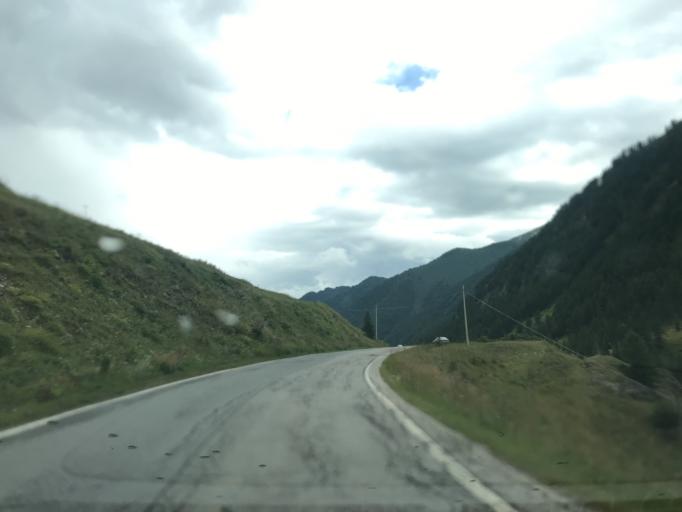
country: IT
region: Piedmont
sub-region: Provincia di Cuneo
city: Pontechianale
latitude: 44.6388
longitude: 7.0113
